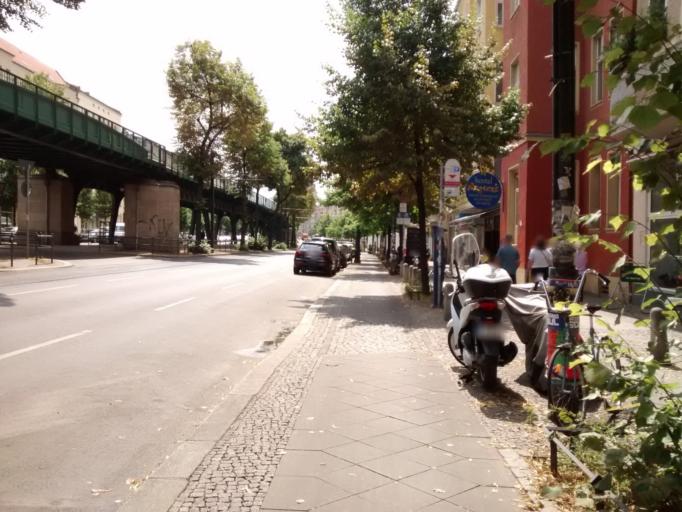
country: DE
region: Berlin
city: Prenzlauer Berg Bezirk
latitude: 52.5447
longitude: 13.4123
